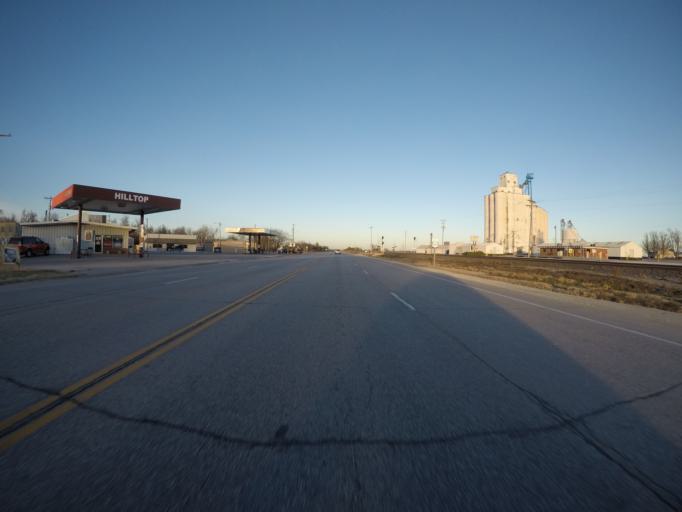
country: US
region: Kansas
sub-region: Harvey County
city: North Newton
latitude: 38.1171
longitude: -97.2566
